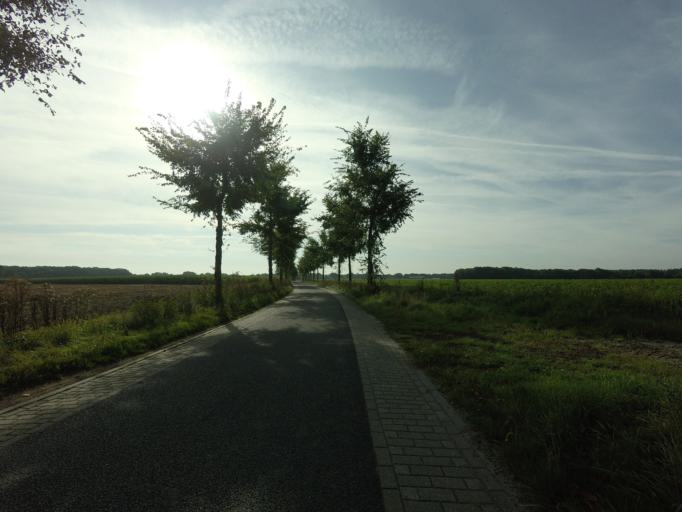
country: NL
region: Drenthe
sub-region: Gemeente Assen
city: Assen
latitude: 53.0029
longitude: 6.6230
